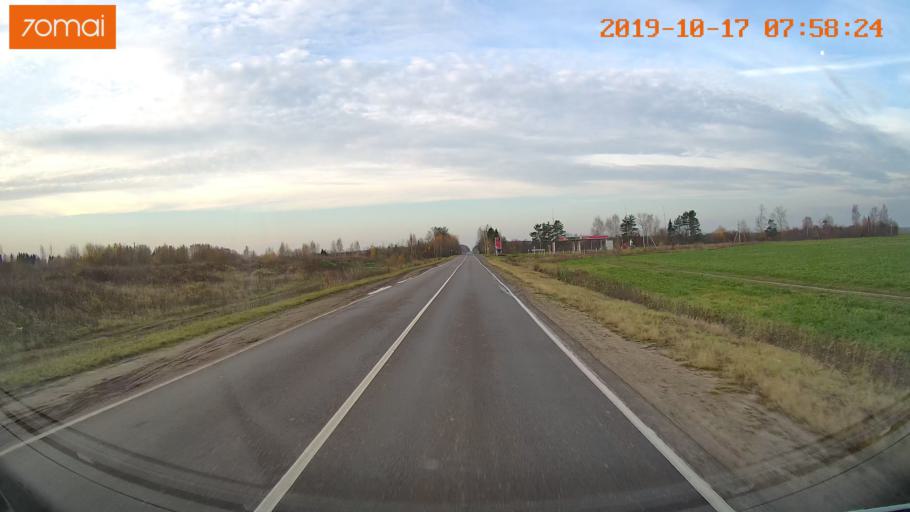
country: RU
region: Vladimir
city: Bavleny
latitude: 56.4030
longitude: 39.5582
